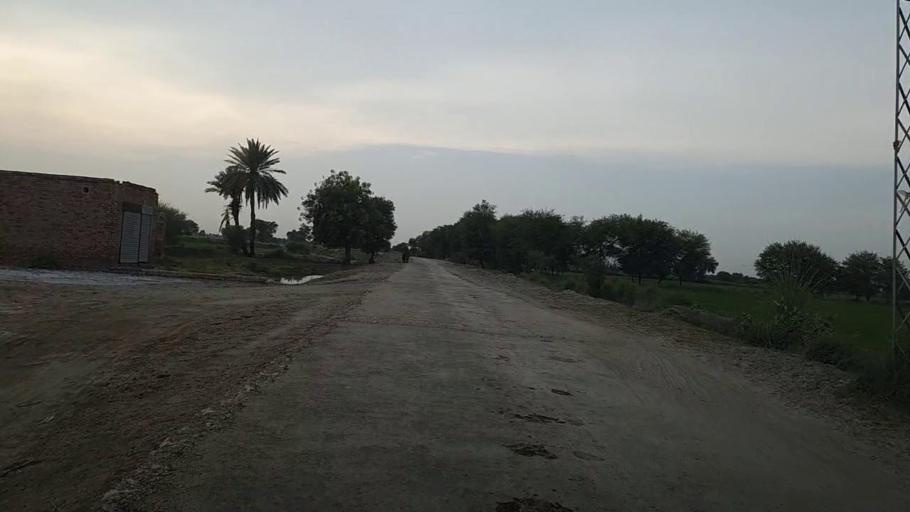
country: PK
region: Sindh
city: Khanpur
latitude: 27.8459
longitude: 69.4581
